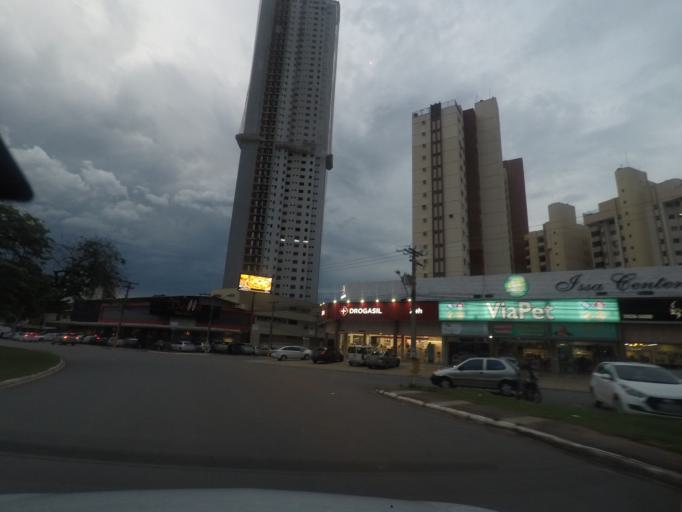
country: BR
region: Goias
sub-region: Goiania
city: Goiania
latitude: -16.7139
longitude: -49.2736
